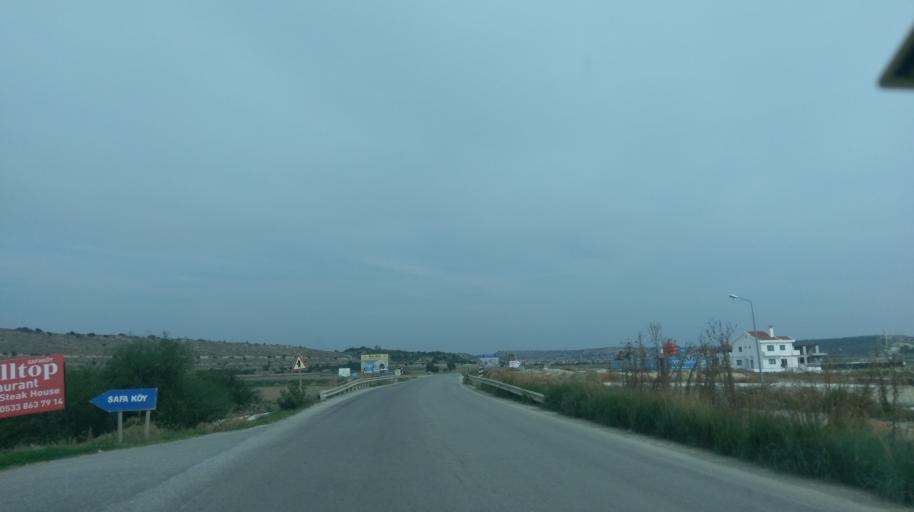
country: CY
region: Ammochostos
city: Trikomo
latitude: 35.3282
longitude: 33.9699
